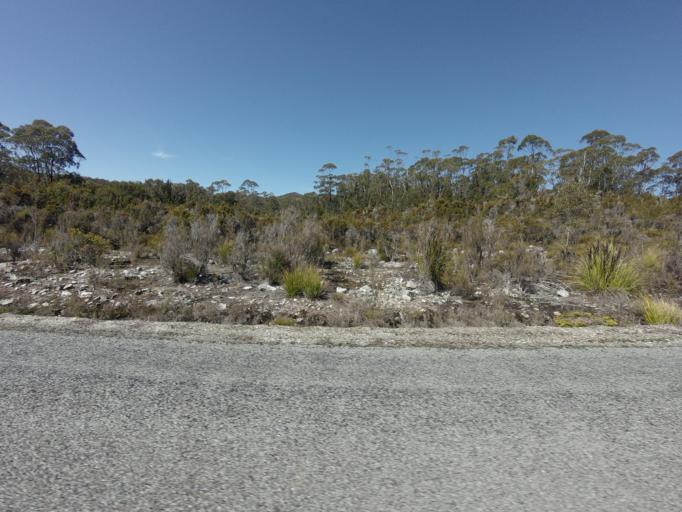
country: AU
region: Tasmania
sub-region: Huon Valley
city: Geeveston
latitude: -42.7706
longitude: 146.3967
